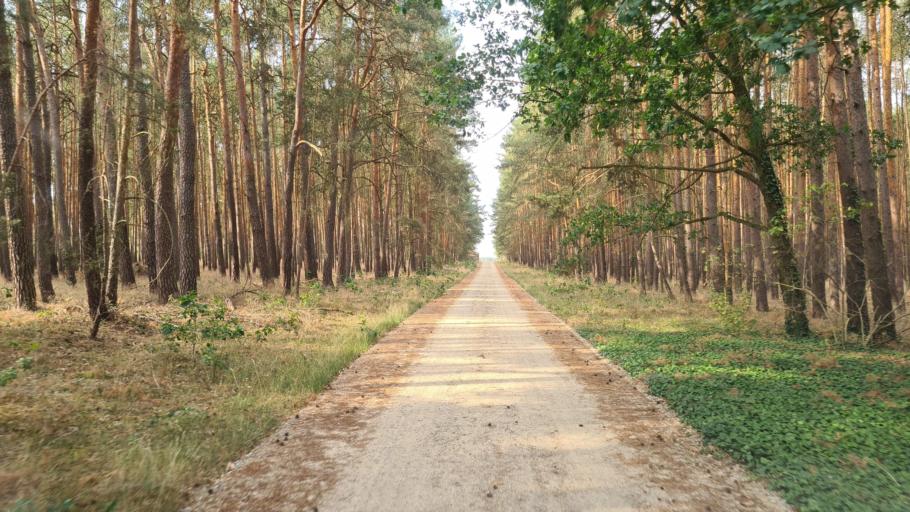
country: DE
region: Brandenburg
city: Linthe
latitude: 52.1126
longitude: 12.8111
